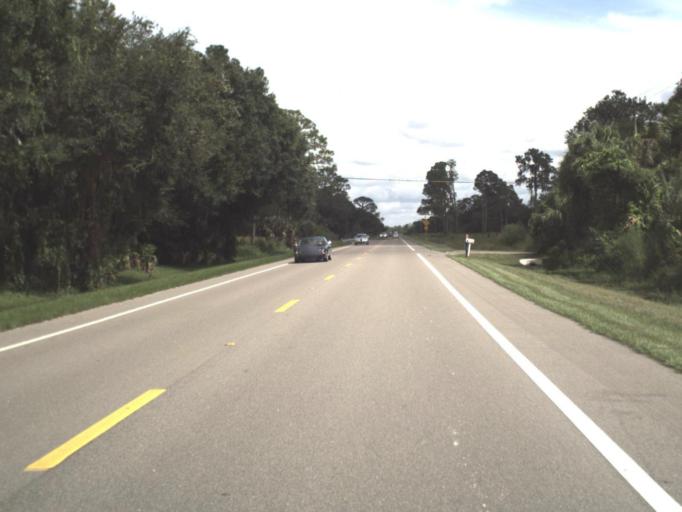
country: US
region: Florida
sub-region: Sarasota County
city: Lake Sarasota
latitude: 27.2449
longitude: -82.3508
